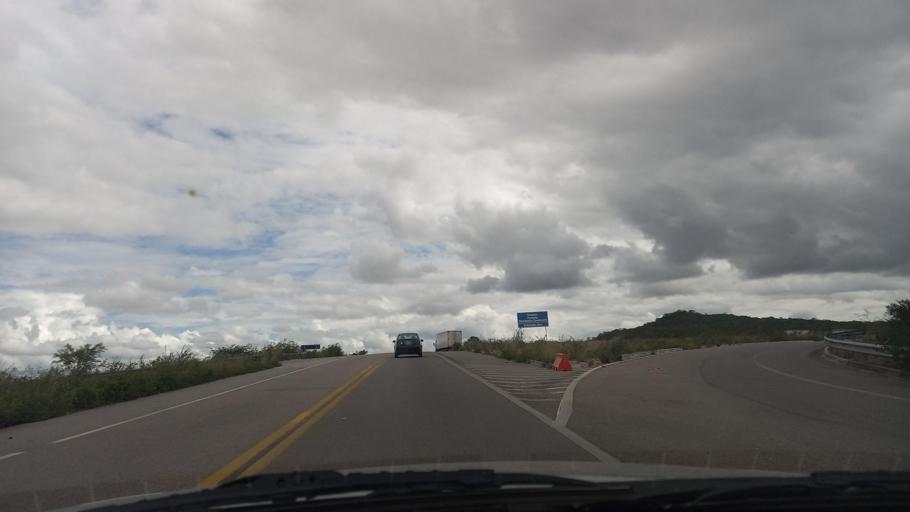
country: BR
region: Pernambuco
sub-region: Caruaru
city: Caruaru
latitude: -8.3286
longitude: -36.1453
